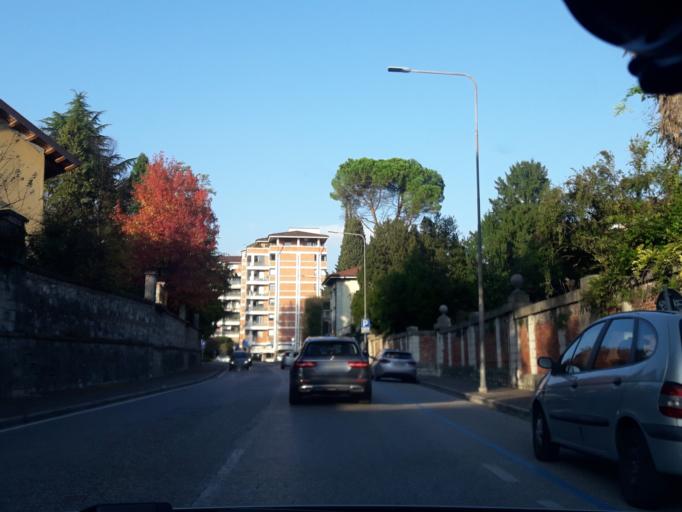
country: IT
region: Friuli Venezia Giulia
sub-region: Provincia di Udine
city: Udine
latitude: 46.0680
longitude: 13.2357
